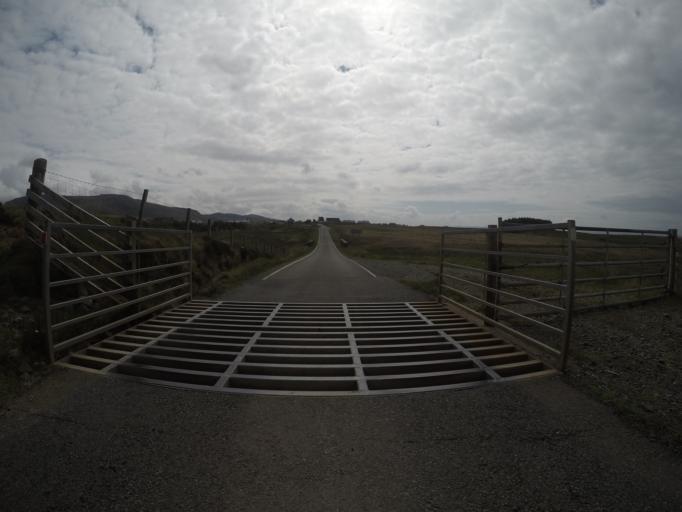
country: GB
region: Scotland
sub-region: Highland
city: Portree
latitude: 57.6509
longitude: -6.3802
